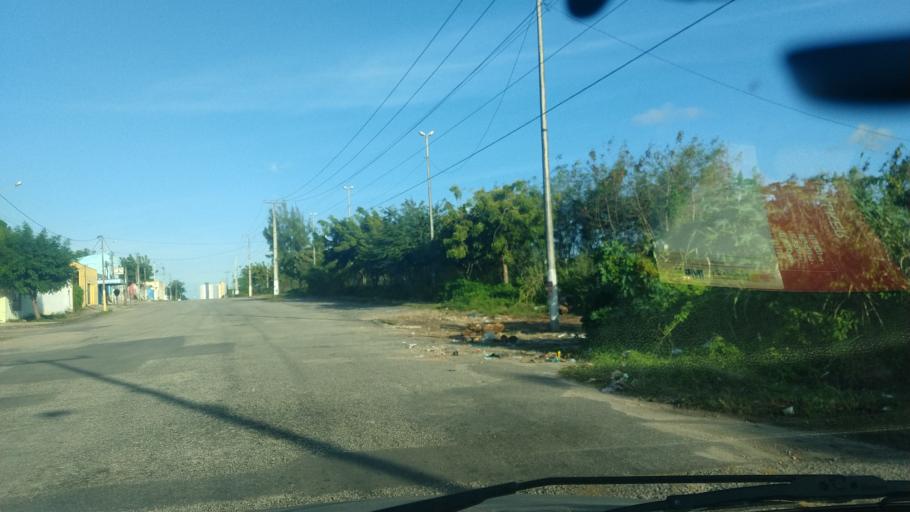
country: BR
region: Rio Grande do Norte
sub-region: Natal
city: Natal
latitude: -5.8737
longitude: -35.1881
